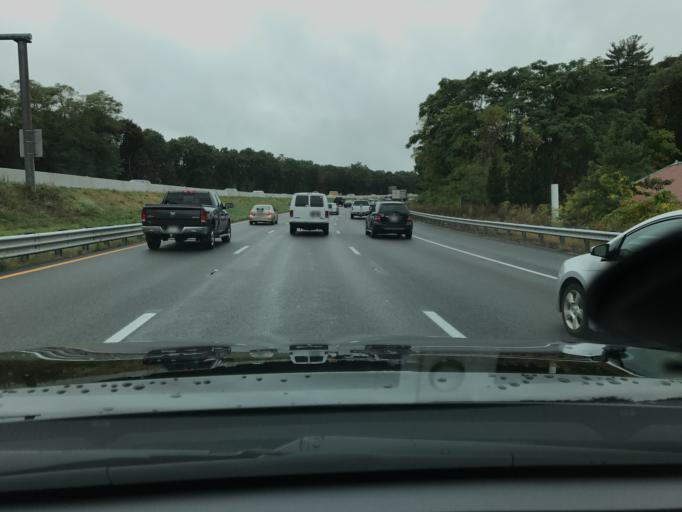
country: US
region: Massachusetts
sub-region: Middlesex County
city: Reading
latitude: 42.5080
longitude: -71.0939
